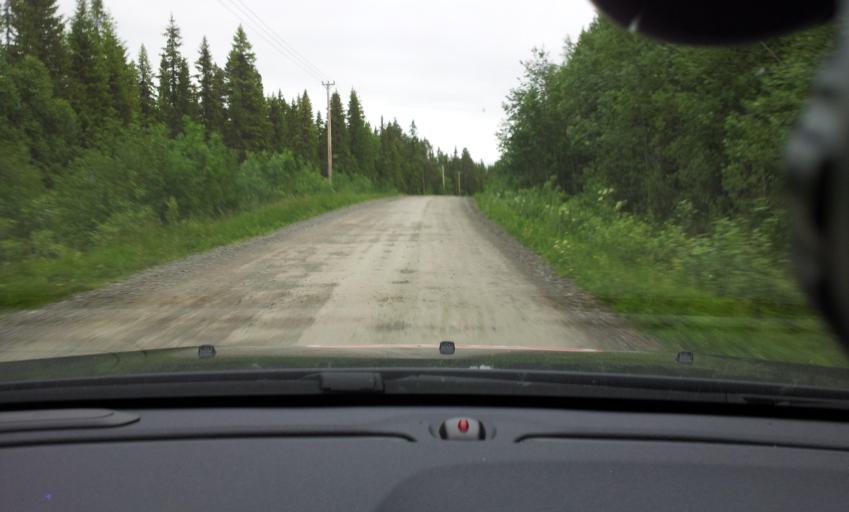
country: SE
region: Jaemtland
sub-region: Are Kommun
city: Jarpen
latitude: 63.2213
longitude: 13.6799
